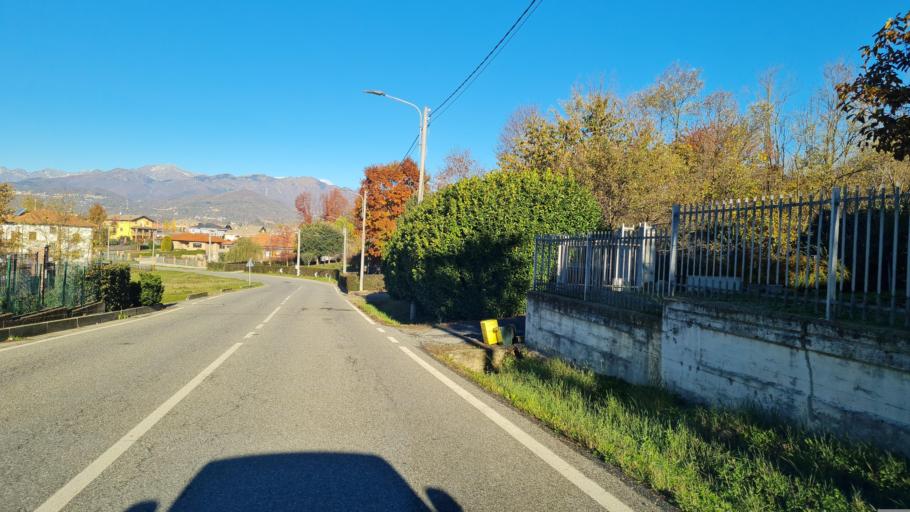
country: IT
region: Piedmont
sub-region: Provincia di Biella
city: Cossato
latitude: 45.5609
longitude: 8.2000
